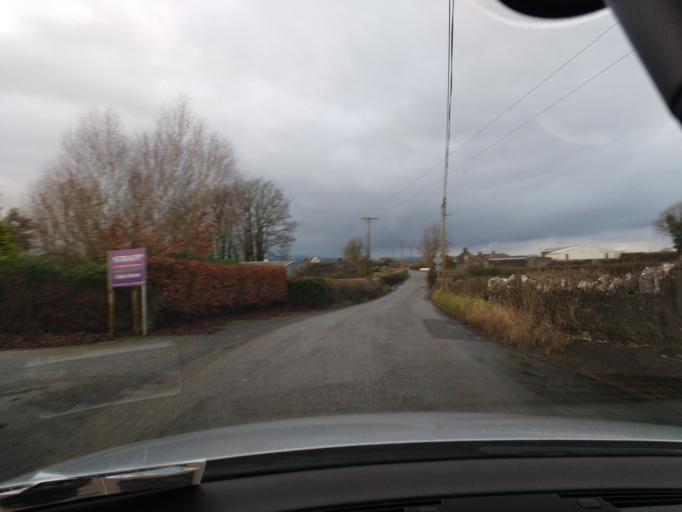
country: IE
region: Munster
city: Thurles
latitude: 52.6375
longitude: -7.8563
